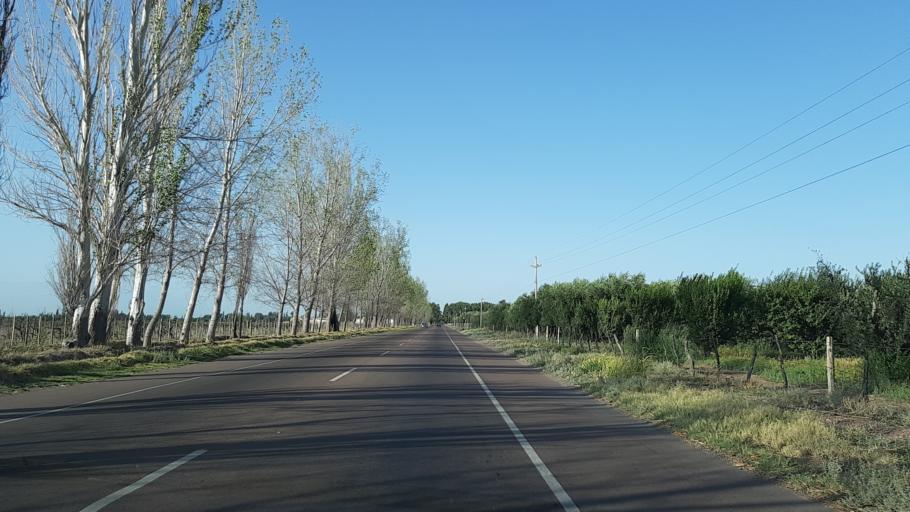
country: AR
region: Mendoza
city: San Martin
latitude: -32.9516
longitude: -68.4300
